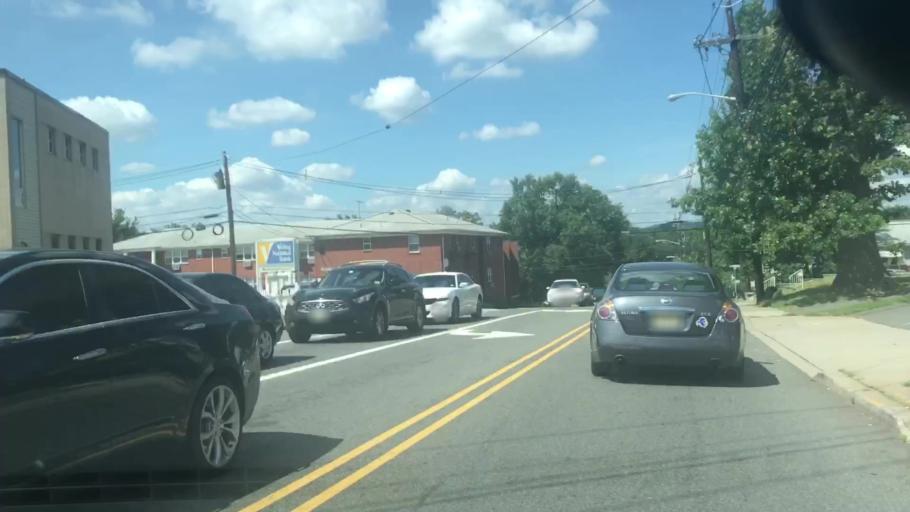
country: US
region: New Jersey
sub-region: Essex County
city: Bloomfield
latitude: 40.8033
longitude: -74.1698
